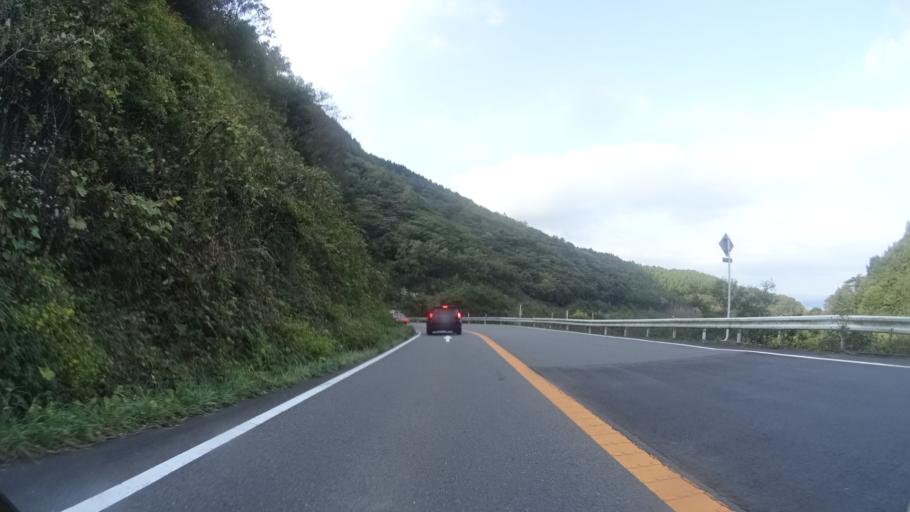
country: JP
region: Oita
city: Beppu
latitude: 33.2805
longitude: 131.4516
